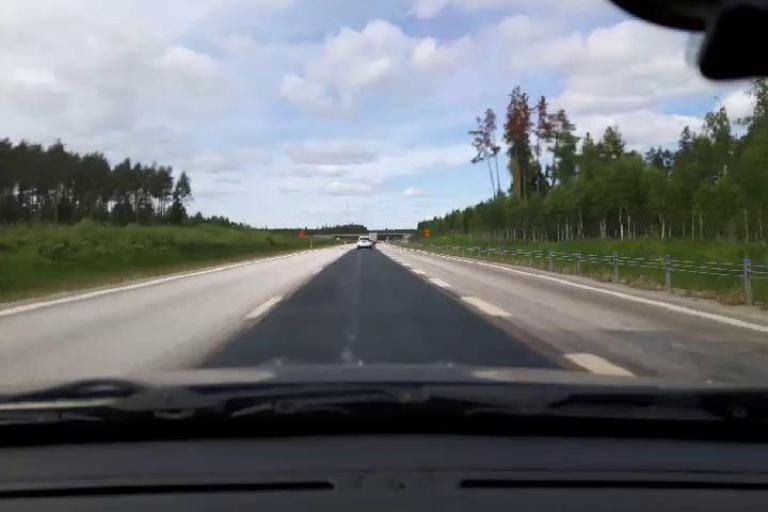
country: SE
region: Uppsala
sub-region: Tierps Kommun
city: Tierp
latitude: 60.4347
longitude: 17.4250
